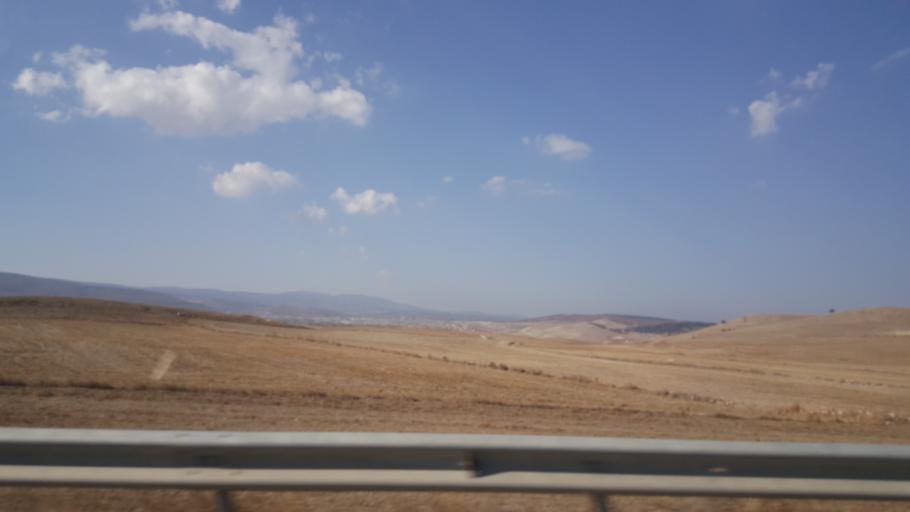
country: TR
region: Eskisehir
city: Kirka
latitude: 39.3131
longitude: 30.5418
